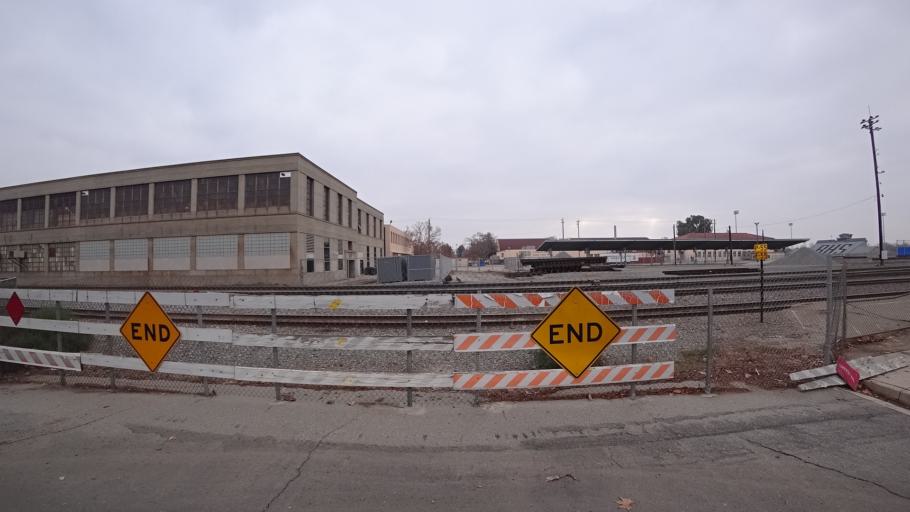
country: US
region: California
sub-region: Kern County
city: Bakersfield
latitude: 35.3716
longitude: -119.0236
